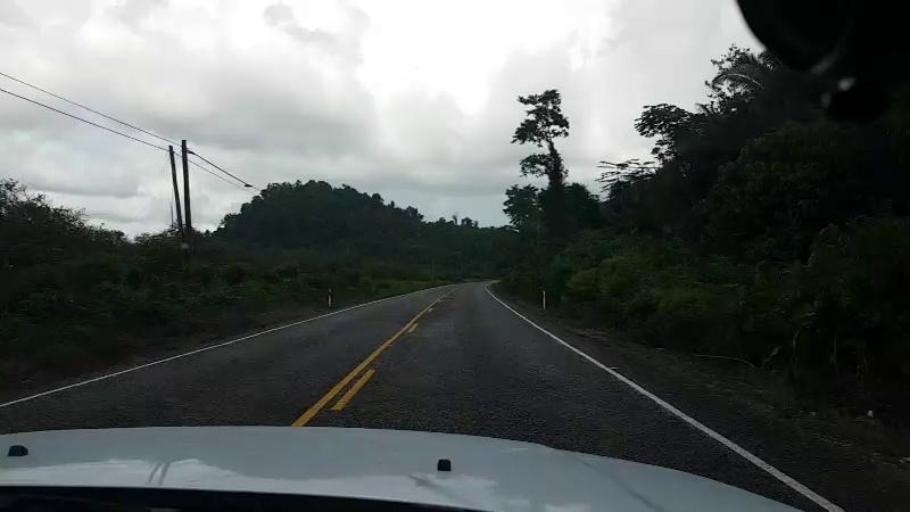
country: BZ
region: Cayo
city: Belmopan
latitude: 17.1551
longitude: -88.6913
